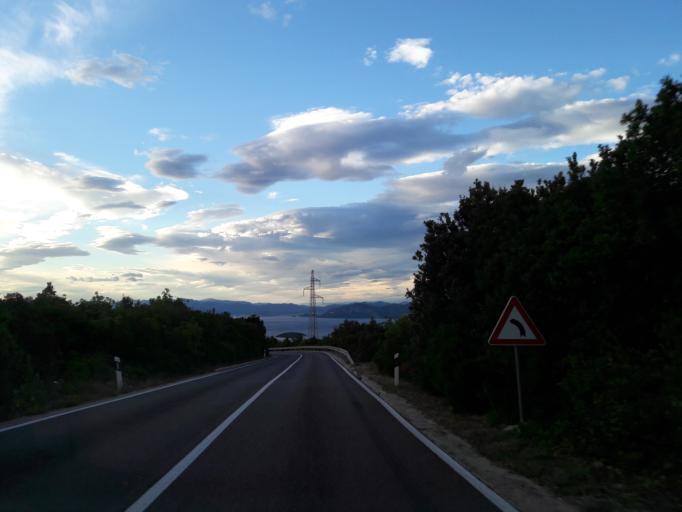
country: BA
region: Federation of Bosnia and Herzegovina
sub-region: Hercegovacko-Bosanski Kanton
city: Neum
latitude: 42.8949
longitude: 17.4948
